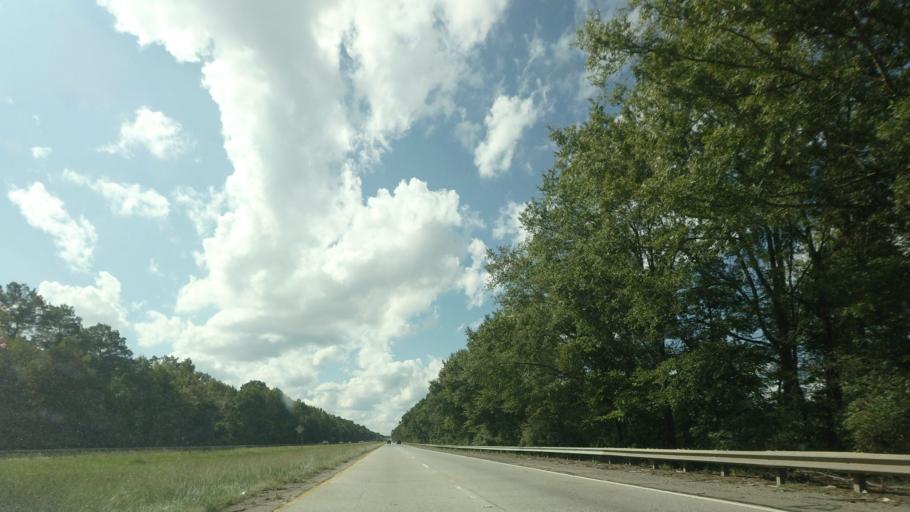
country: US
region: Georgia
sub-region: Bibb County
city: Macon
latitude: 32.8159
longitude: -83.5826
